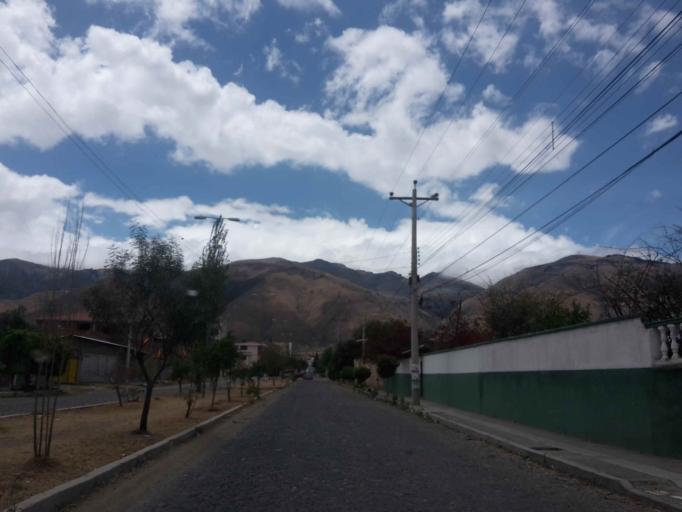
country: BO
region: Cochabamba
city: Cochabamba
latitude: -17.3470
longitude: -66.1972
